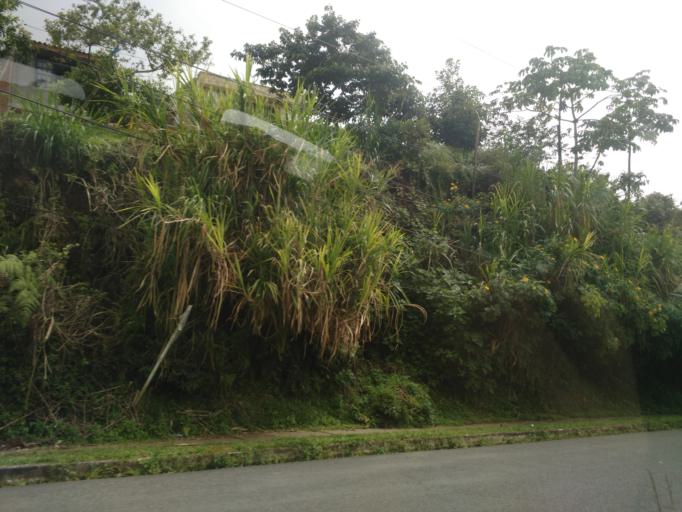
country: CO
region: Valle del Cauca
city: Sevilla
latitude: 4.2665
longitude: -75.9275
